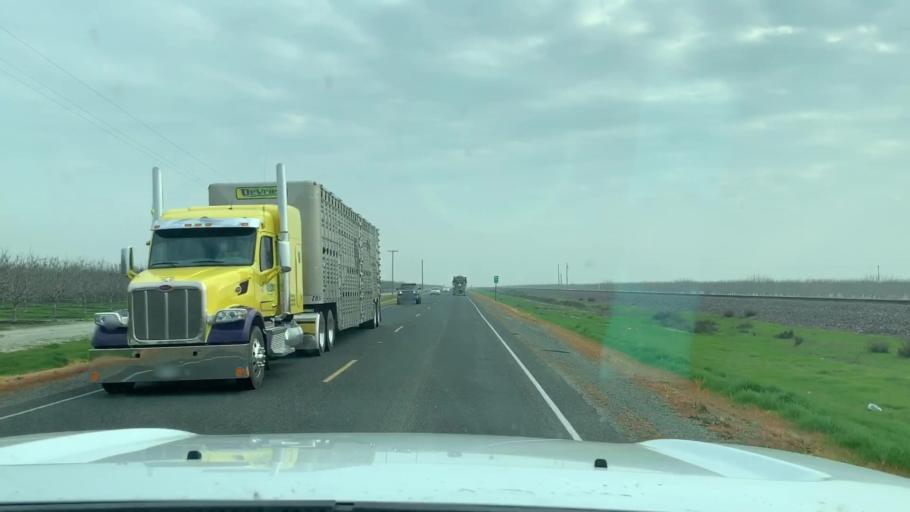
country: US
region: California
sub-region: Tulare County
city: Earlimart
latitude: 35.8219
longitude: -119.3661
